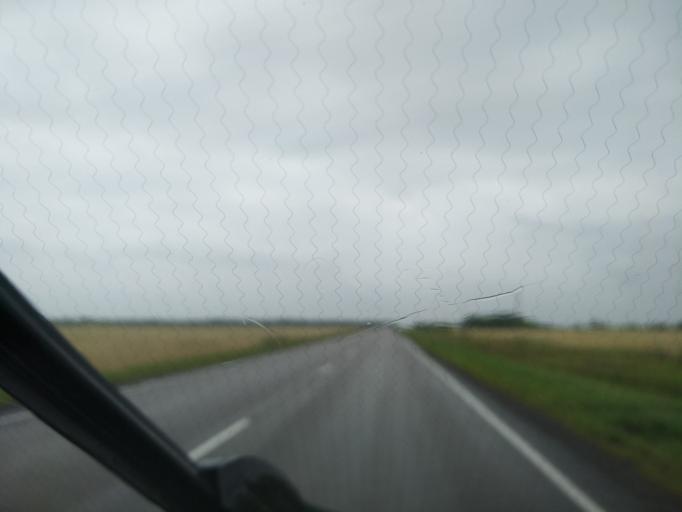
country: RU
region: Voronezj
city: Orlovo
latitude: 51.6764
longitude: 39.7713
